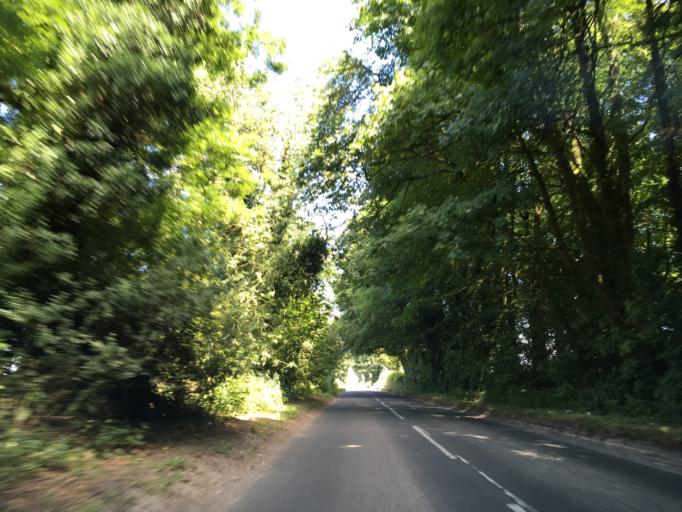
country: GB
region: England
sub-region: Gloucestershire
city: Stroud
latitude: 51.7481
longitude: -2.1830
